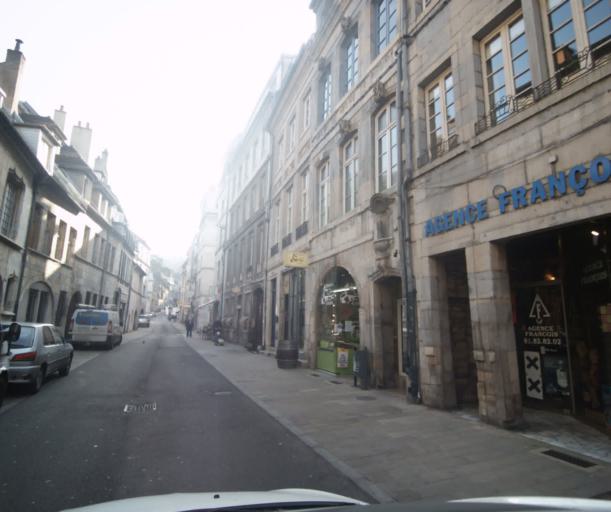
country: FR
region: Franche-Comte
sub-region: Departement du Doubs
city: Besancon
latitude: 47.2353
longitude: 6.0283
